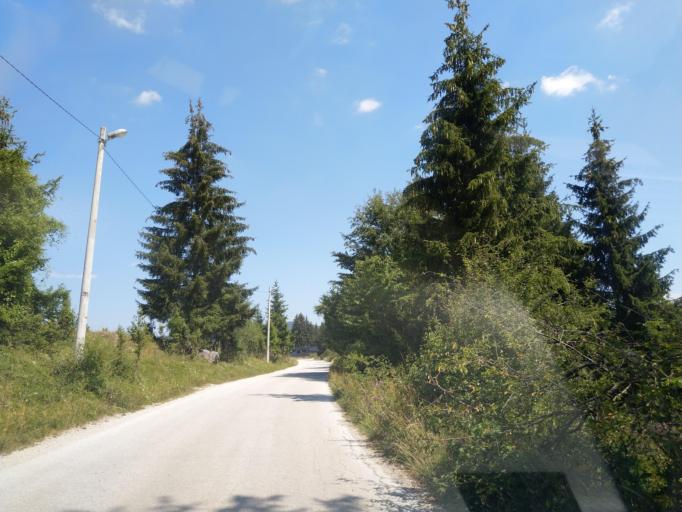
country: RS
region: Central Serbia
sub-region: Zlatiborski Okrug
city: Nova Varos
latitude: 43.4669
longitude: 19.9719
